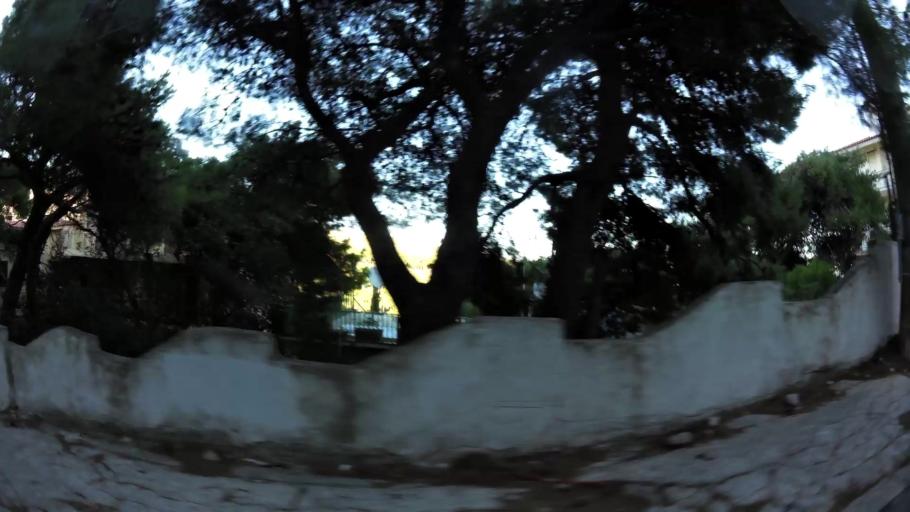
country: GR
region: Attica
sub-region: Nomarchia Athinas
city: Penteli
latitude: 38.0495
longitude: 23.8664
